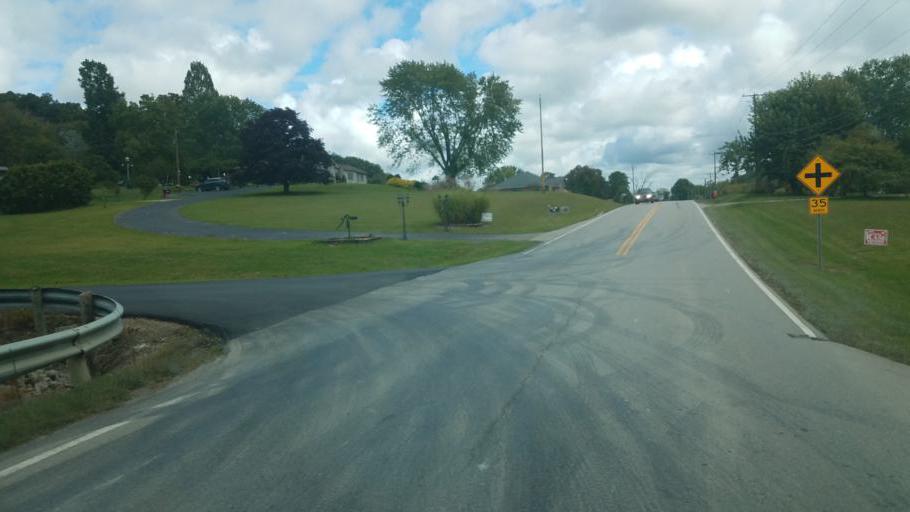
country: US
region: Ohio
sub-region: Scioto County
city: Lucasville
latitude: 38.8659
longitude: -82.8860
